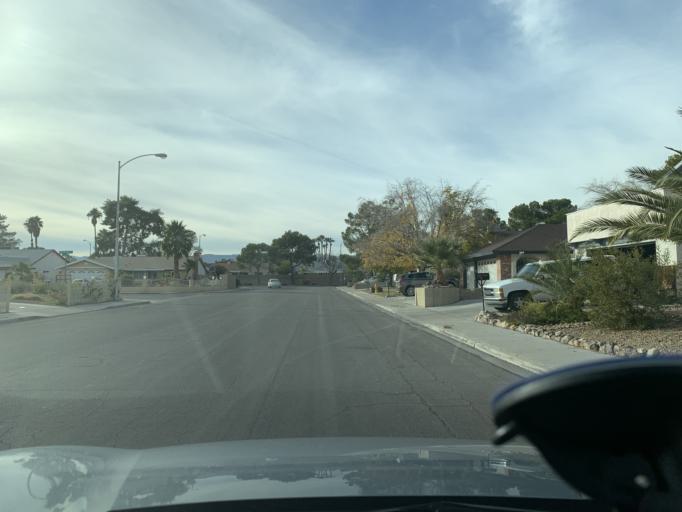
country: US
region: Nevada
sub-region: Clark County
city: Spring Valley
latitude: 36.1092
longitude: -115.2368
